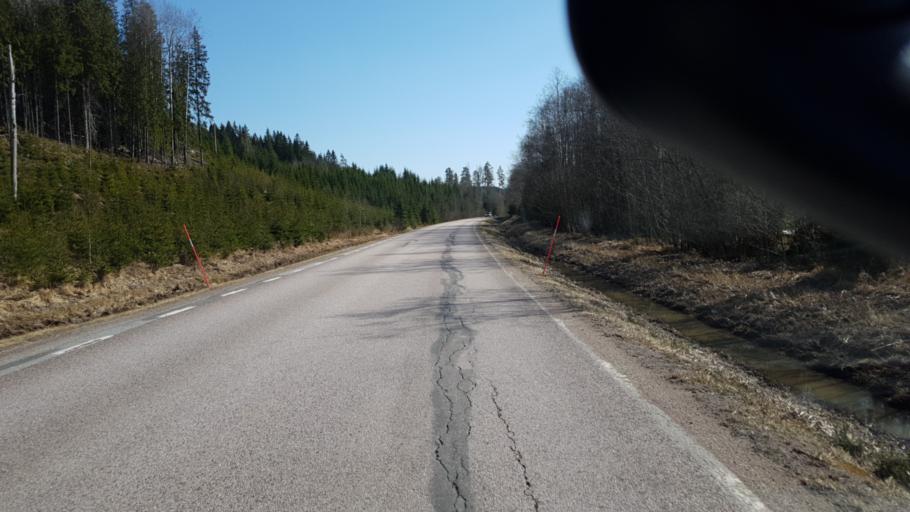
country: SE
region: Vaermland
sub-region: Arvika Kommun
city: Arvika
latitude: 59.6796
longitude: 12.7951
